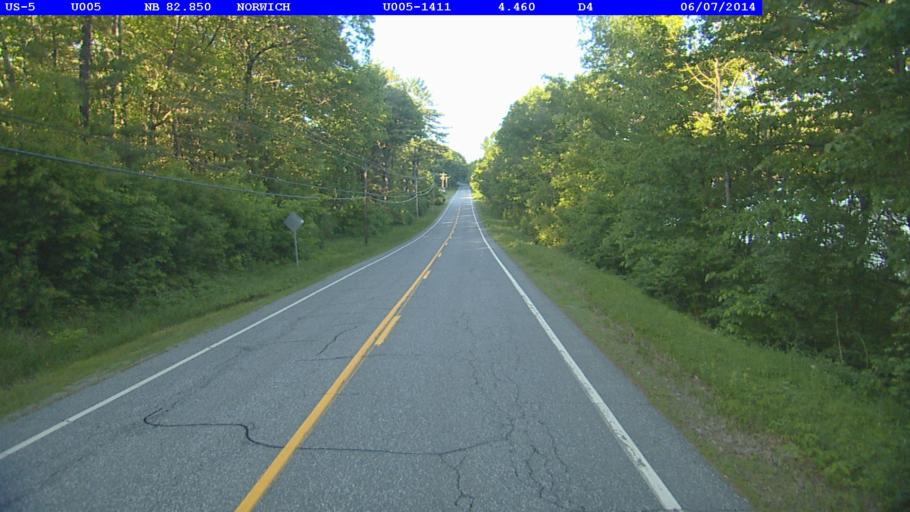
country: US
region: New Hampshire
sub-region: Grafton County
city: Hanover
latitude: 43.7361
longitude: -72.2615
